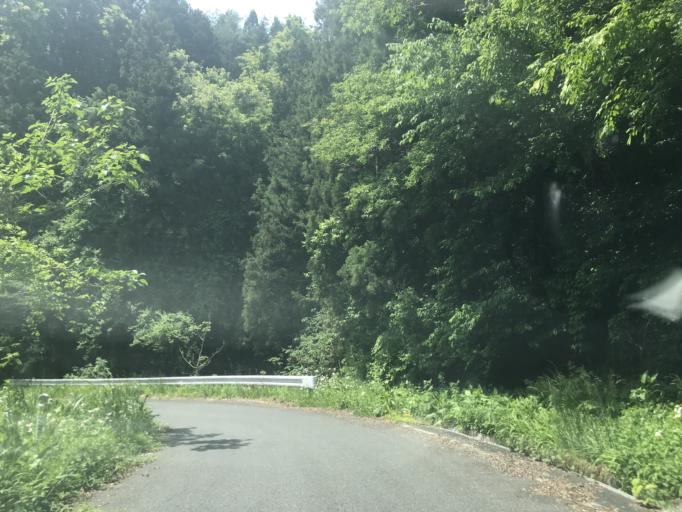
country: JP
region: Iwate
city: Ichinoseki
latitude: 38.9659
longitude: 141.2324
